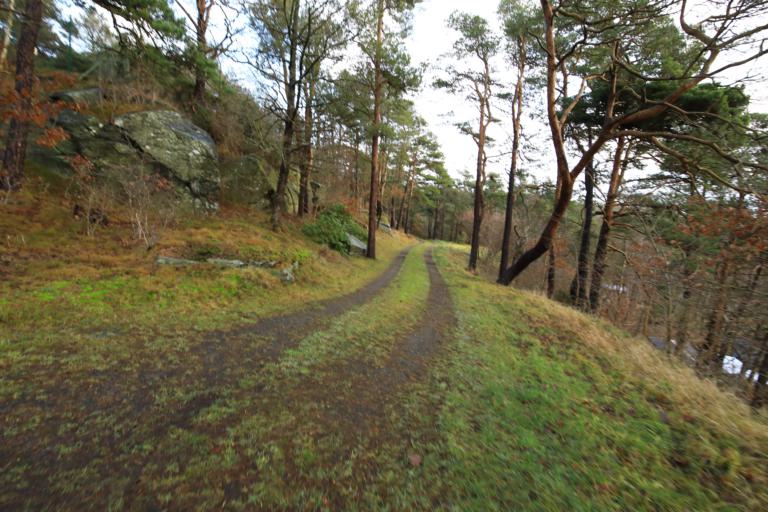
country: SE
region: Halland
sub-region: Varbergs Kommun
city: Varberg
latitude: 57.1484
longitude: 12.2814
